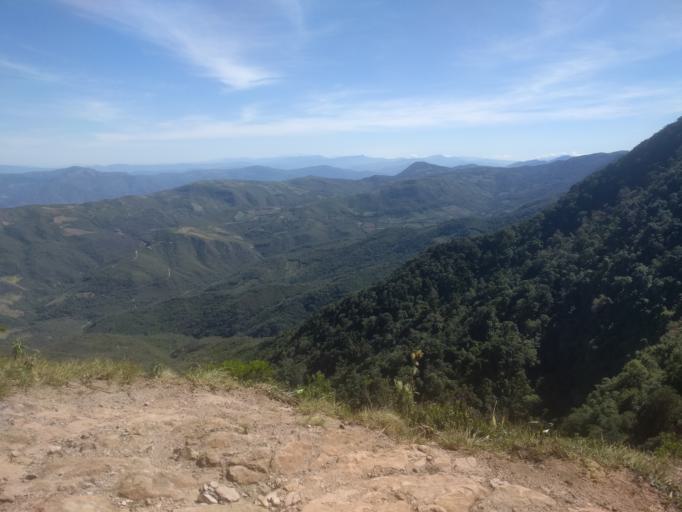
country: BO
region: Santa Cruz
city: Samaipata
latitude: -18.1107
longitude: -63.8744
